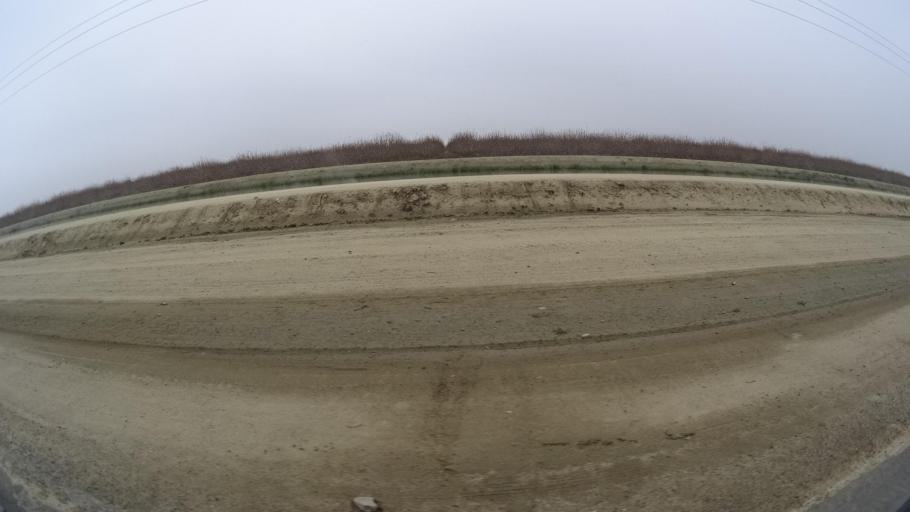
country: US
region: California
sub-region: Kern County
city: Wasco
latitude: 35.6982
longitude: -119.4017
